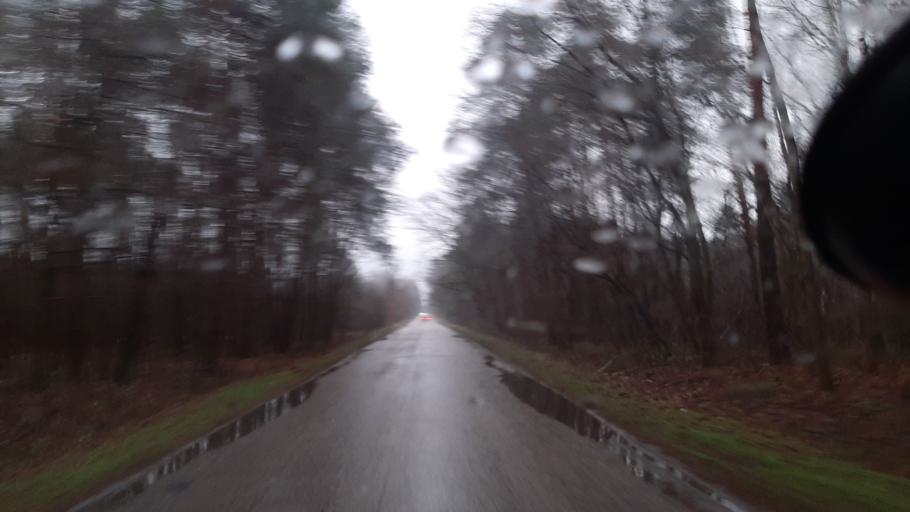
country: PL
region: Lublin Voivodeship
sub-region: Powiat lubartowski
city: Kamionka
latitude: 51.5058
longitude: 22.4891
